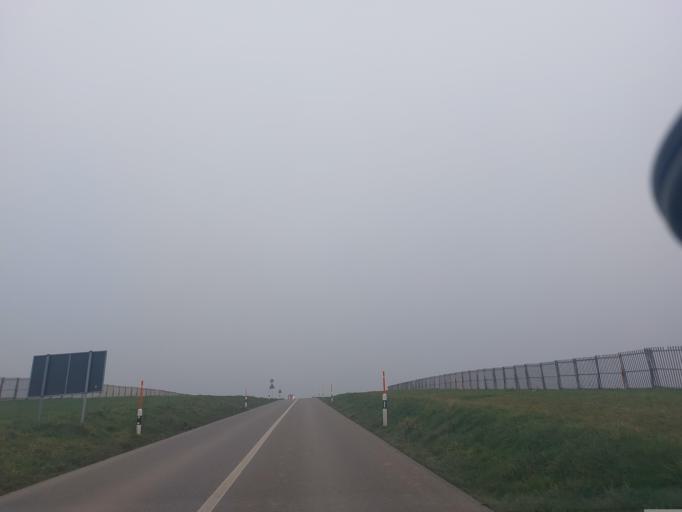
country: CH
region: Vaud
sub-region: Lavaux-Oron District
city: Oron-la-ville
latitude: 46.5755
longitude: 6.8588
